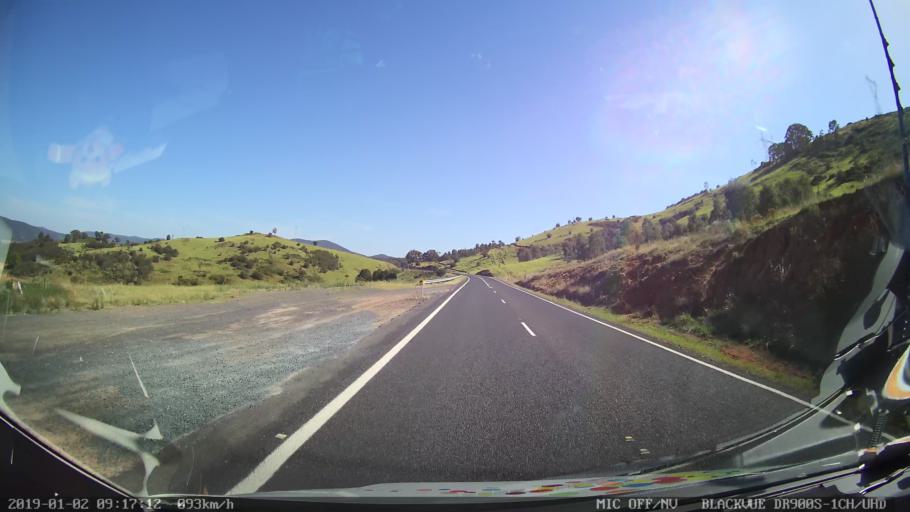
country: AU
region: New South Wales
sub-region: Tumut Shire
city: Tumut
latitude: -35.4443
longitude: 148.2868
